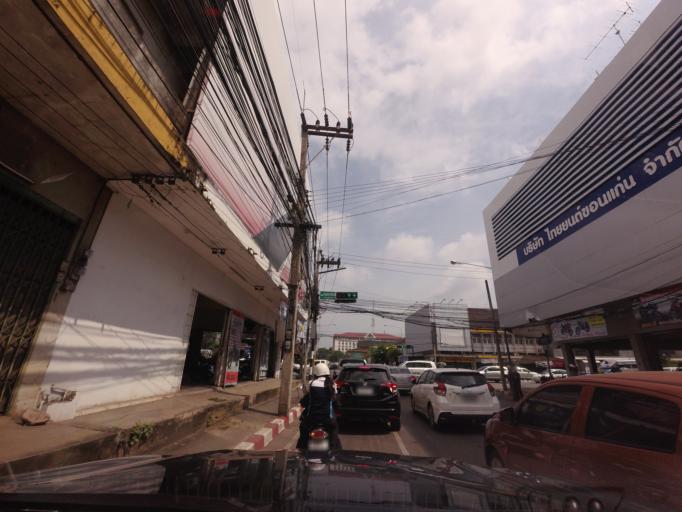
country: TH
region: Khon Kaen
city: Khon Kaen
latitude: 16.4390
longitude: 102.8307
